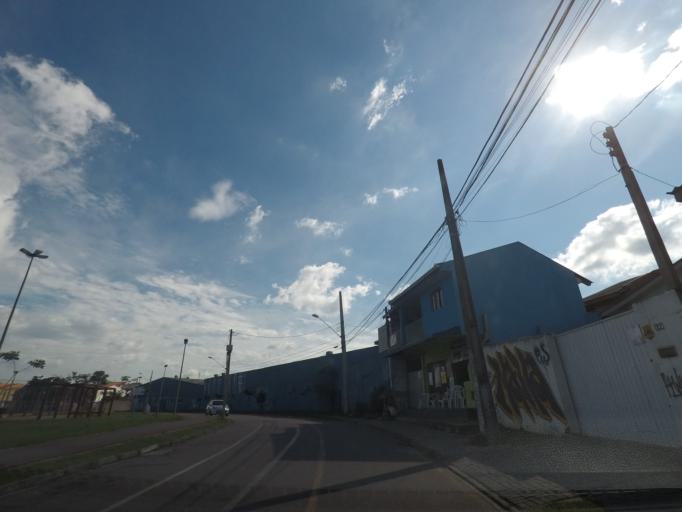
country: BR
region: Parana
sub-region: Curitiba
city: Curitiba
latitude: -25.4782
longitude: -49.3337
